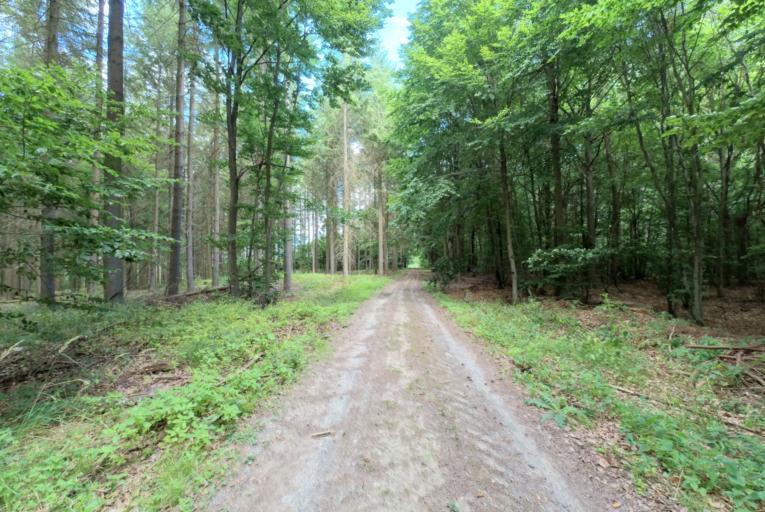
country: DE
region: Baden-Wuerttemberg
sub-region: Karlsruhe Region
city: Fahrenbach
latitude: 49.4164
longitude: 9.1154
